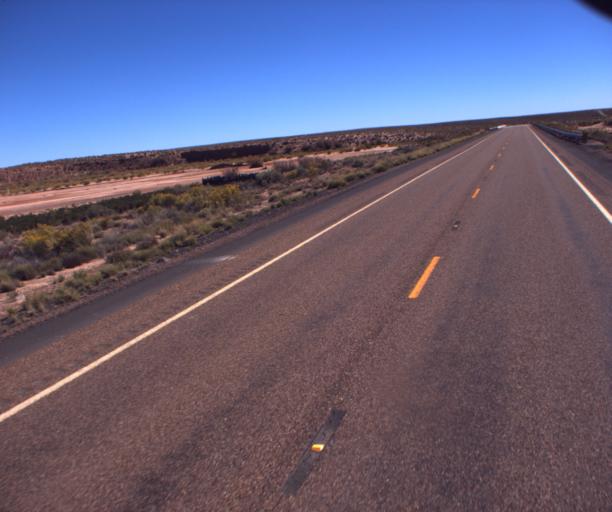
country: US
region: Arizona
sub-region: Navajo County
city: Holbrook
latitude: 35.0657
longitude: -110.0989
